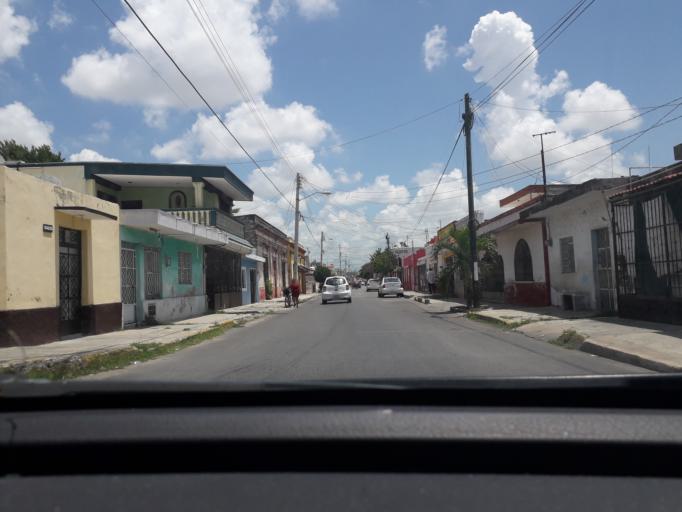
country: MX
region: Yucatan
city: Merida
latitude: 20.9547
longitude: -89.6206
